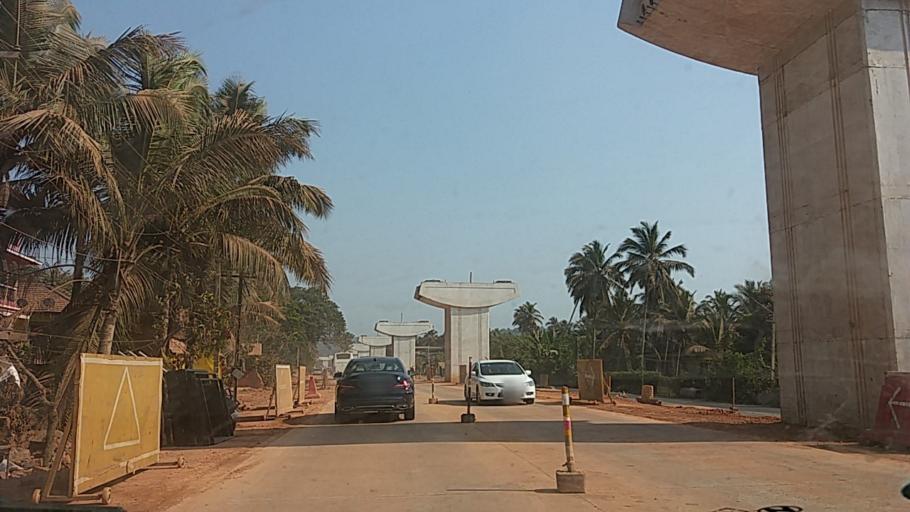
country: IN
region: Goa
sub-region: South Goa
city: Cortalim
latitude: 15.4012
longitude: 73.9086
